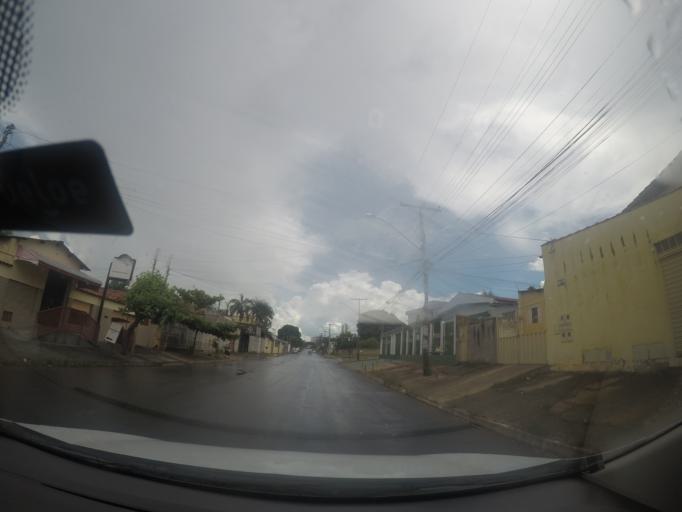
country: BR
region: Goias
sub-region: Goiania
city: Goiania
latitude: -16.6968
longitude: -49.2938
